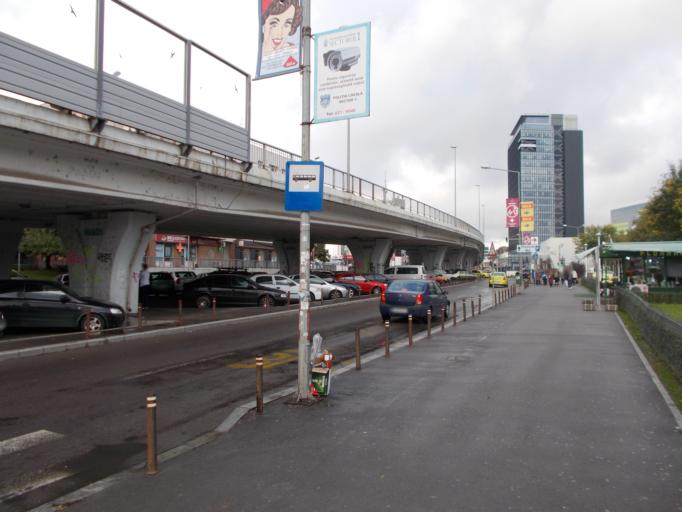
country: RO
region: Bucuresti
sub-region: Municipiul Bucuresti
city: Bucharest
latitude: 44.4795
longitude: 26.1003
